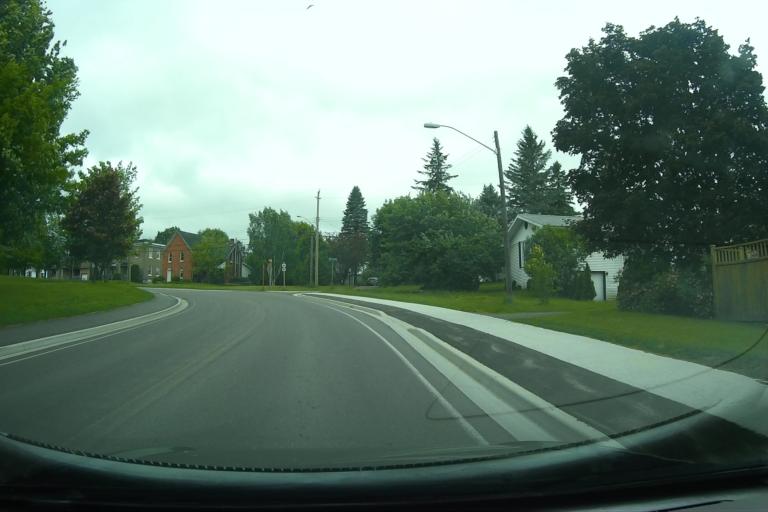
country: CA
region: Ontario
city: Pembroke
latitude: 45.5349
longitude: -77.0979
